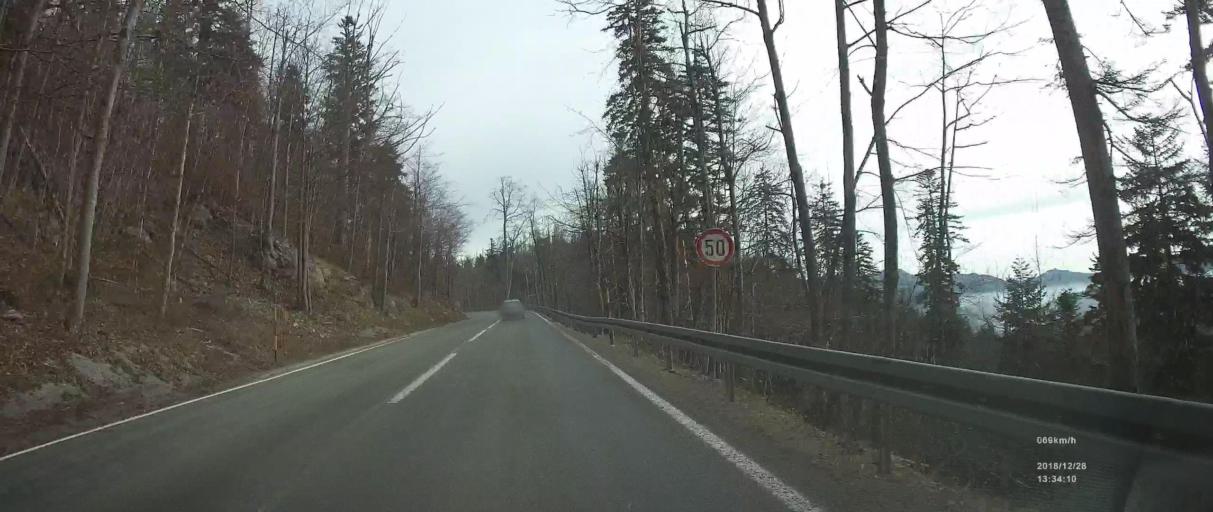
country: HR
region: Primorsko-Goranska
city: Hreljin
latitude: 45.3401
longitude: 14.6882
